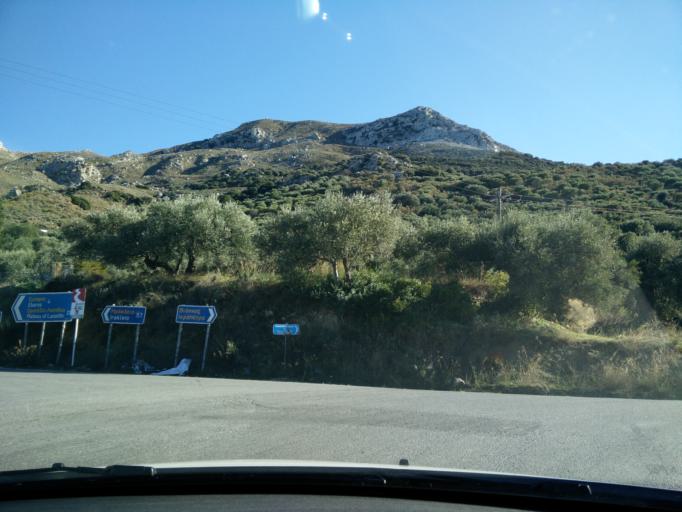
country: GR
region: Crete
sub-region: Nomos Irakleiou
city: Arkalochori
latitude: 35.0790
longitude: 25.3633
